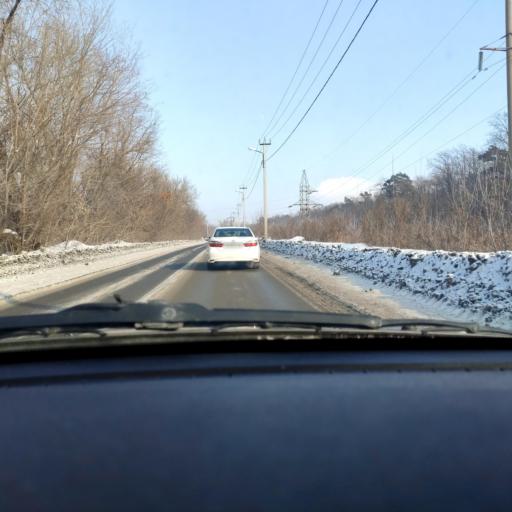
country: RU
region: Samara
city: Zhigulevsk
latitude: 53.5114
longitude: 49.4654
